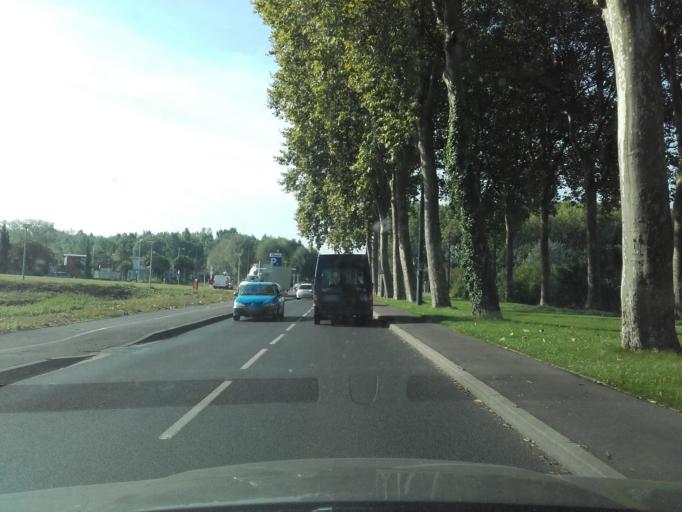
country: FR
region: Centre
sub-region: Departement d'Indre-et-Loire
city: Joue-les-Tours
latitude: 47.3665
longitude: 0.6755
